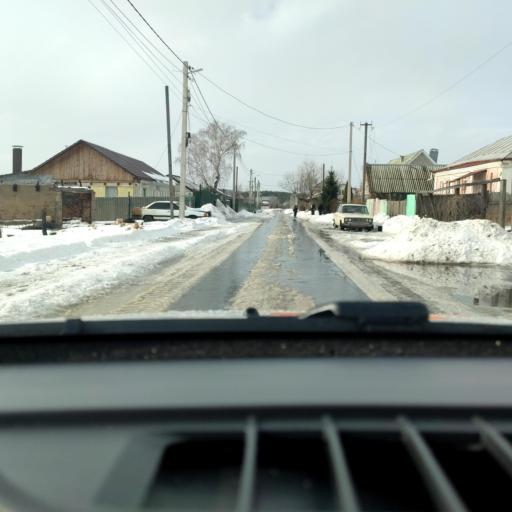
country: RU
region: Voronezj
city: Podgornoye
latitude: 51.7684
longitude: 39.1065
